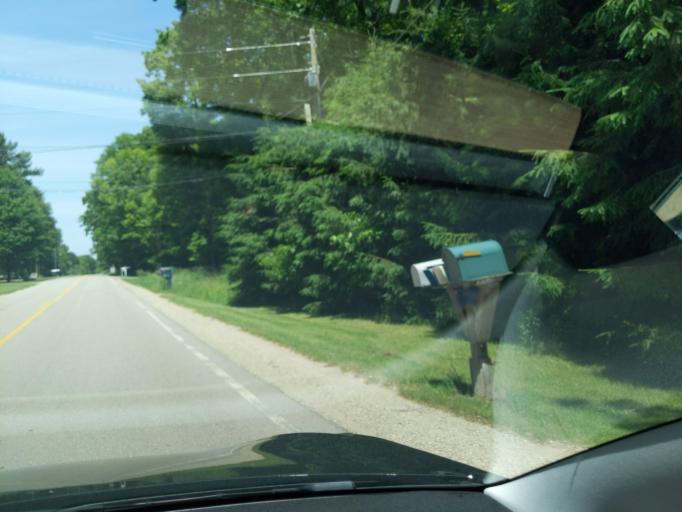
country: US
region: Michigan
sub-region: Muskegon County
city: Montague
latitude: 43.4114
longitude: -86.4166
